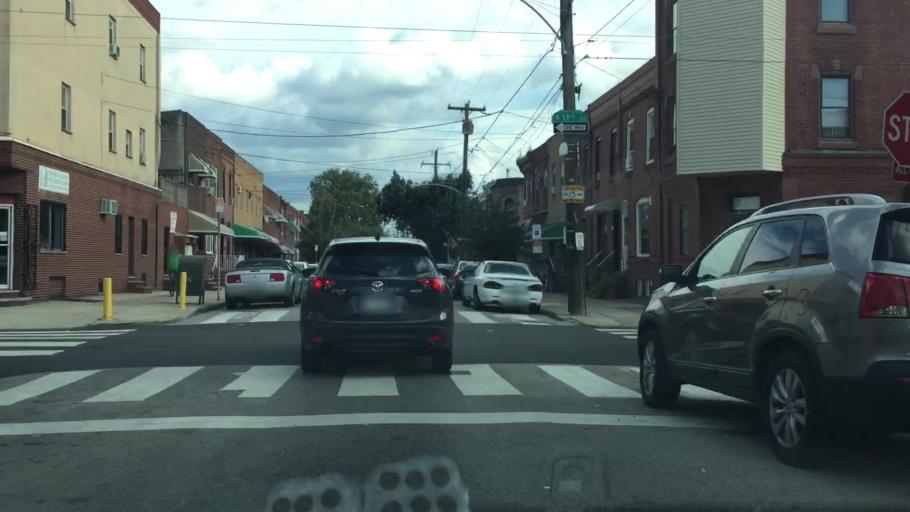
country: US
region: Pennsylvania
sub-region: Philadelphia County
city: Philadelphia
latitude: 39.9212
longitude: -75.1652
